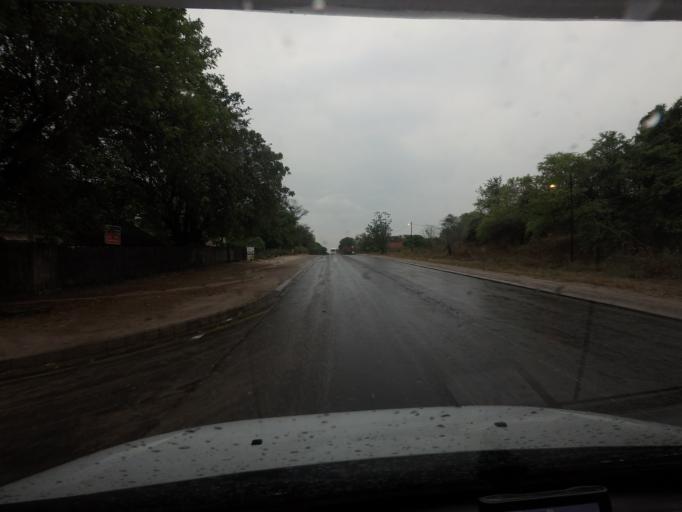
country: ZM
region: Western
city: Sesheke
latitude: -17.4893
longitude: 24.2855
